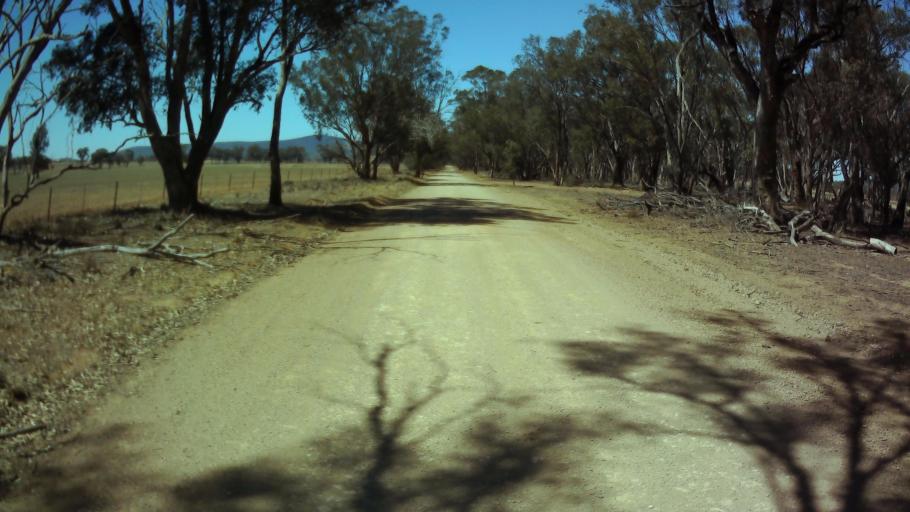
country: AU
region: New South Wales
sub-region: Weddin
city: Grenfell
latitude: -33.8982
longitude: 148.0838
